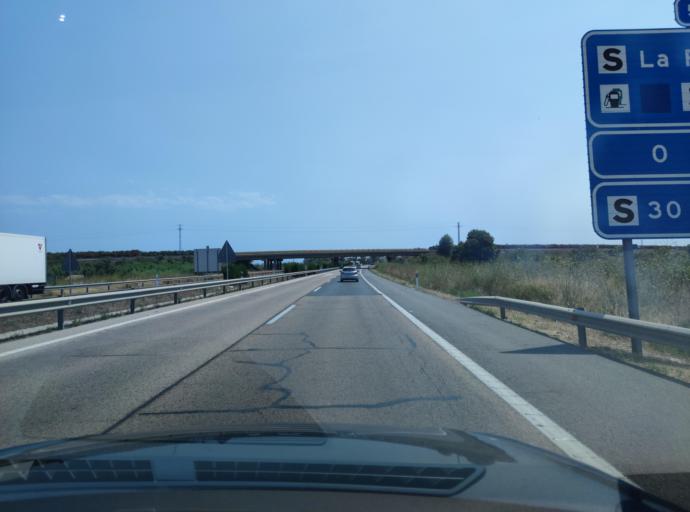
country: ES
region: Valencia
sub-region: Provincia de Castello
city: Alquerias del Nino Perdido
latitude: 39.8733
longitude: -0.1225
